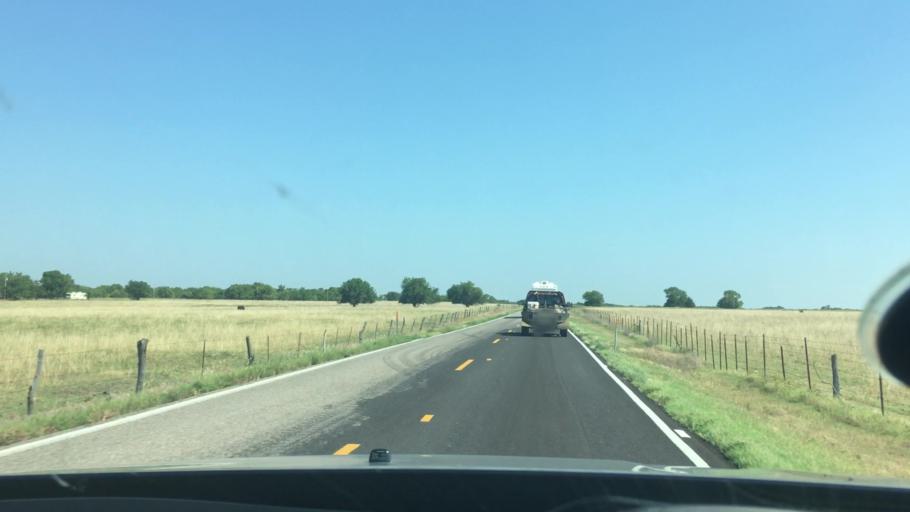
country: US
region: Oklahoma
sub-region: Johnston County
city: Tishomingo
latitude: 34.1764
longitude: -96.5111
